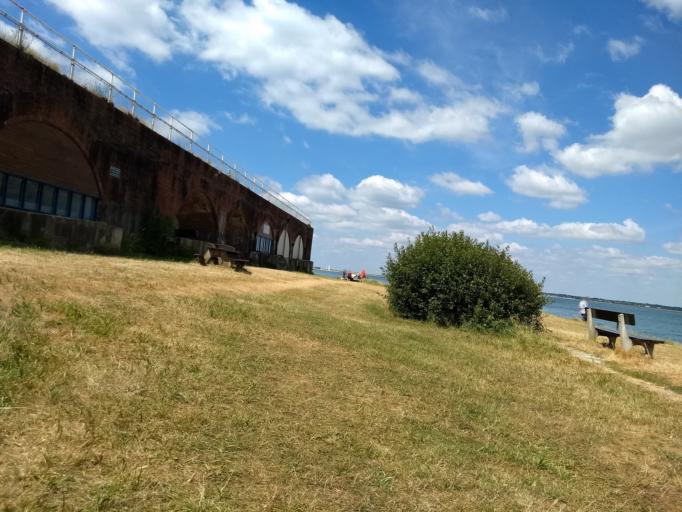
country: GB
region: England
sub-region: Isle of Wight
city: Freshwater
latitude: 50.7070
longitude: -1.5210
